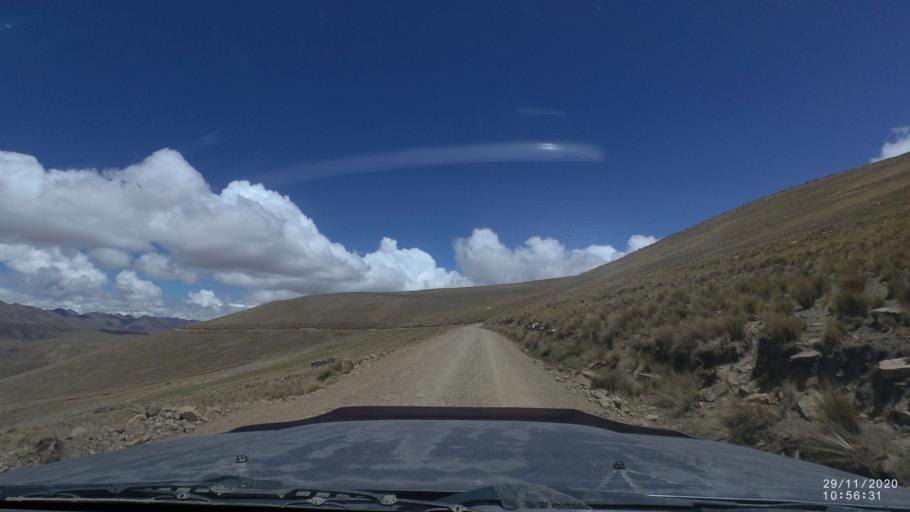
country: BO
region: Cochabamba
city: Cochabamba
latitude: -17.2190
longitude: -66.2247
